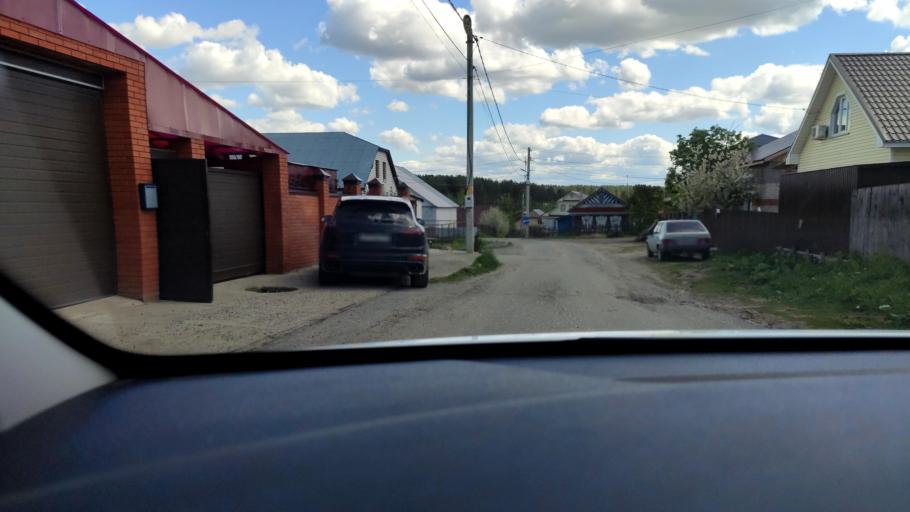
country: RU
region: Tatarstan
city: Stolbishchi
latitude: 55.7025
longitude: 49.1528
